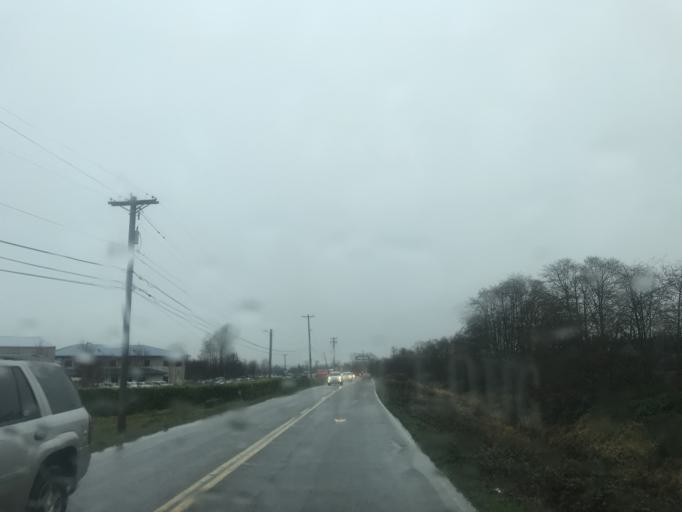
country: US
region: Washington
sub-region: Pierce County
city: Fife
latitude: 47.2134
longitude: -122.3392
